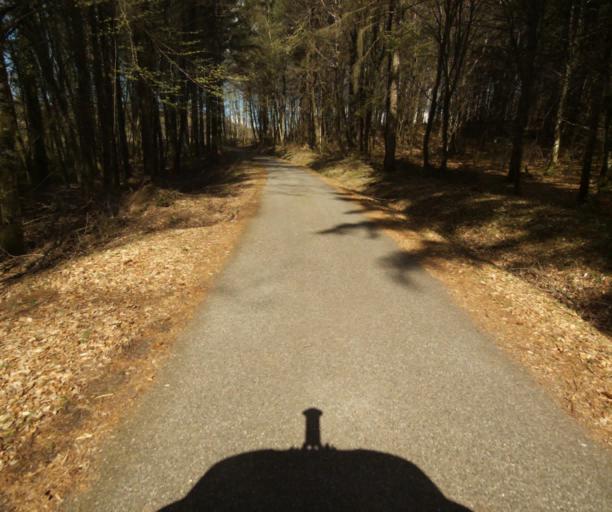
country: FR
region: Limousin
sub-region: Departement de la Correze
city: Argentat
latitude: 45.2362
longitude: 1.9407
